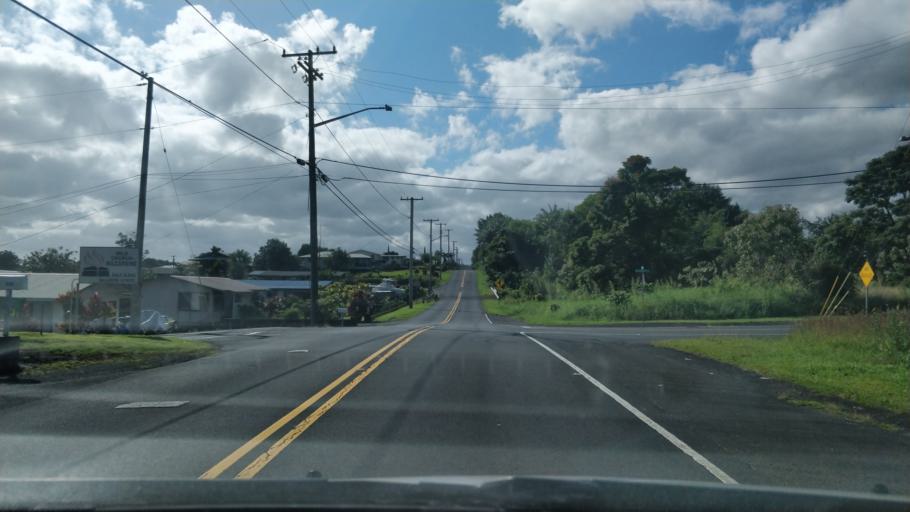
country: US
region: Hawaii
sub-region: Hawaii County
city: Hilo
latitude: 19.6764
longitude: -155.1061
